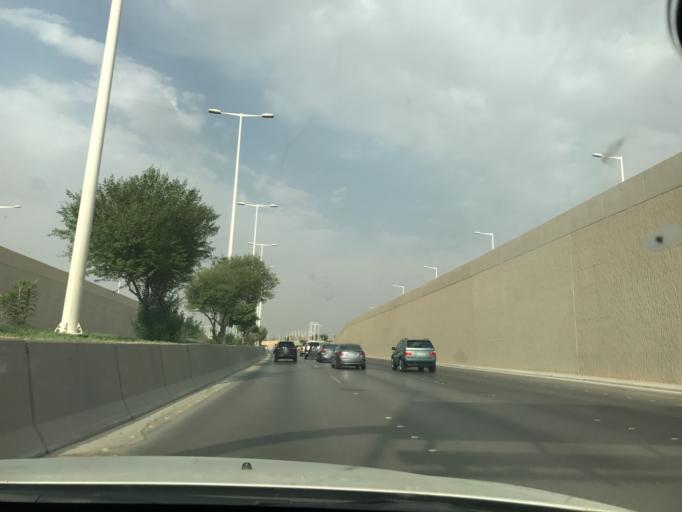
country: SA
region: Ar Riyad
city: Riyadh
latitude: 24.7338
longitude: 46.7378
